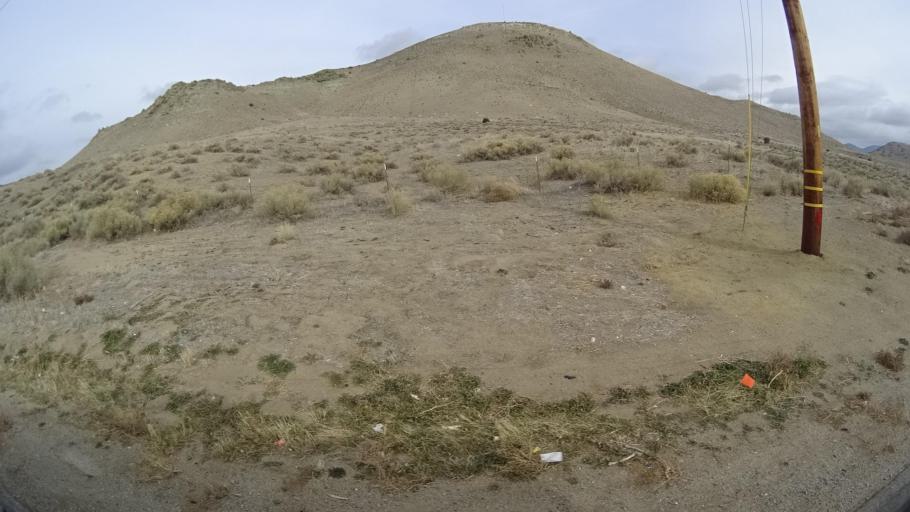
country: US
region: California
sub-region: Kern County
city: Tehachapi
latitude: 35.1217
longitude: -118.3512
